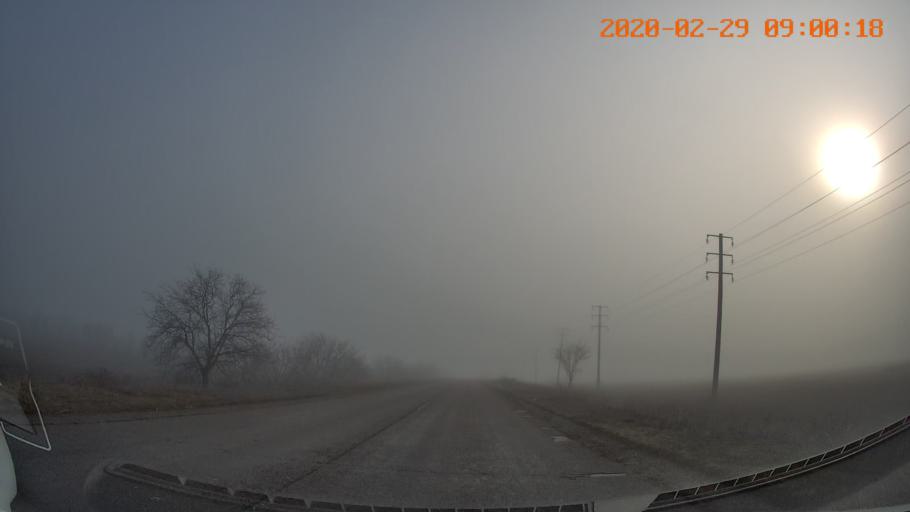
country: UA
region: Odessa
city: Velykoploske
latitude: 46.9219
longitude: 29.6736
